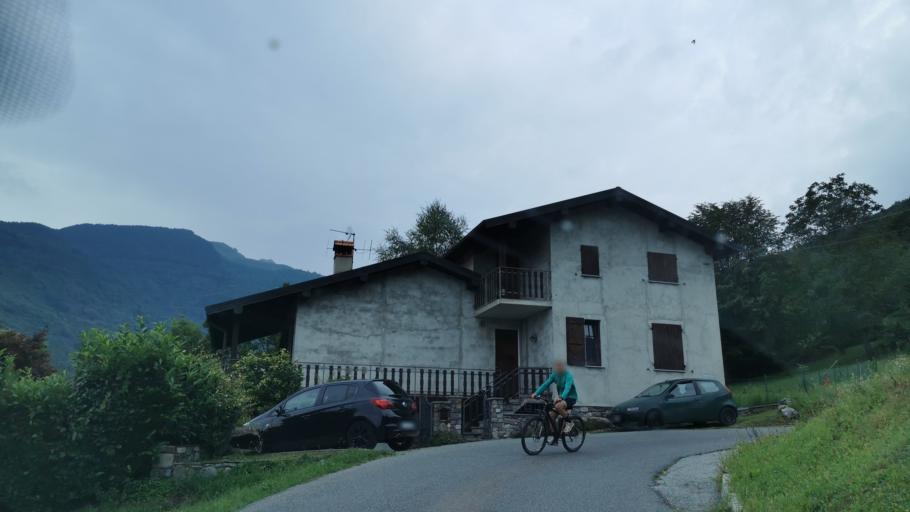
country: IT
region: Lombardy
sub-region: Provincia di Como
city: Dosso del Liro
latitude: 46.1621
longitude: 9.2737
